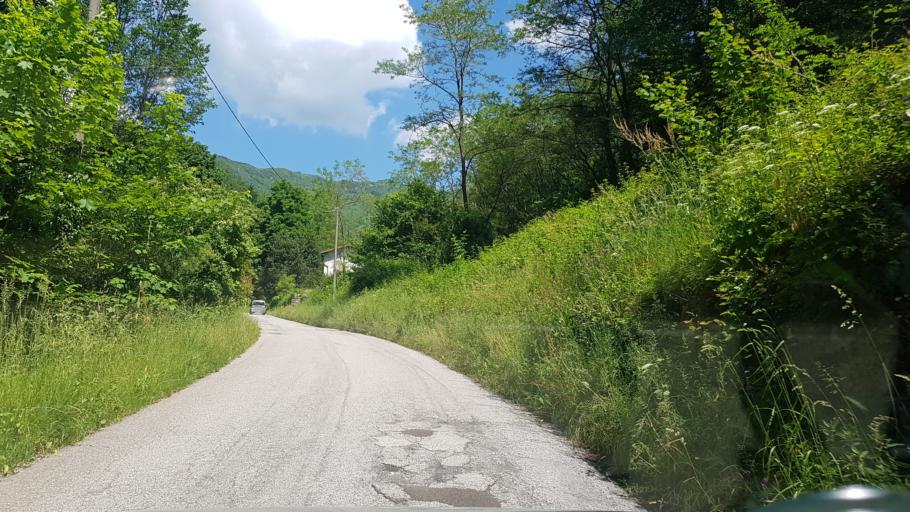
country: IT
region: Friuli Venezia Giulia
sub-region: Provincia di Udine
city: Torreano
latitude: 46.1564
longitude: 13.4321
